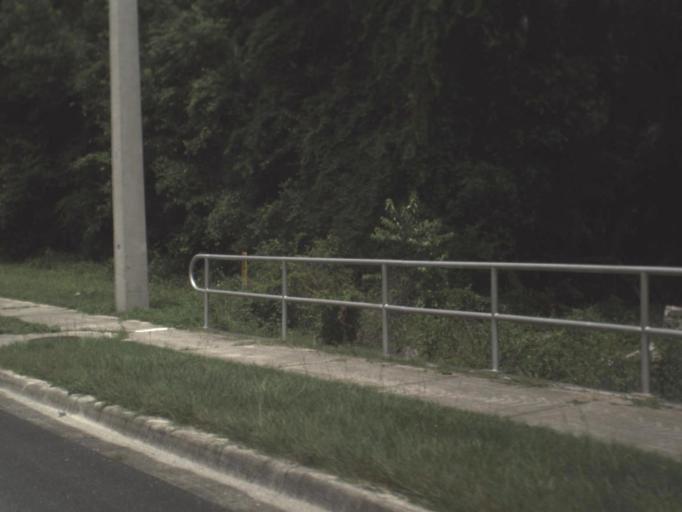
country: US
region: Florida
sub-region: Alachua County
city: Newberry
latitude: 29.6542
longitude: -82.5251
